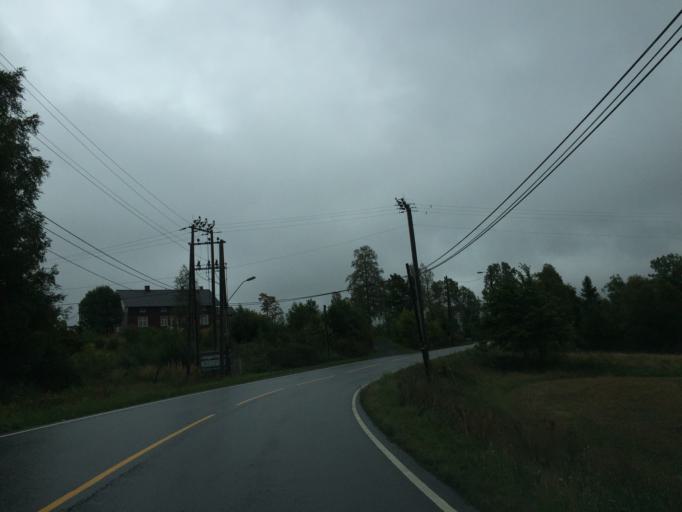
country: NO
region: Akershus
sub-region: Baerum
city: Lysaker
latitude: 60.0051
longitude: 10.6193
